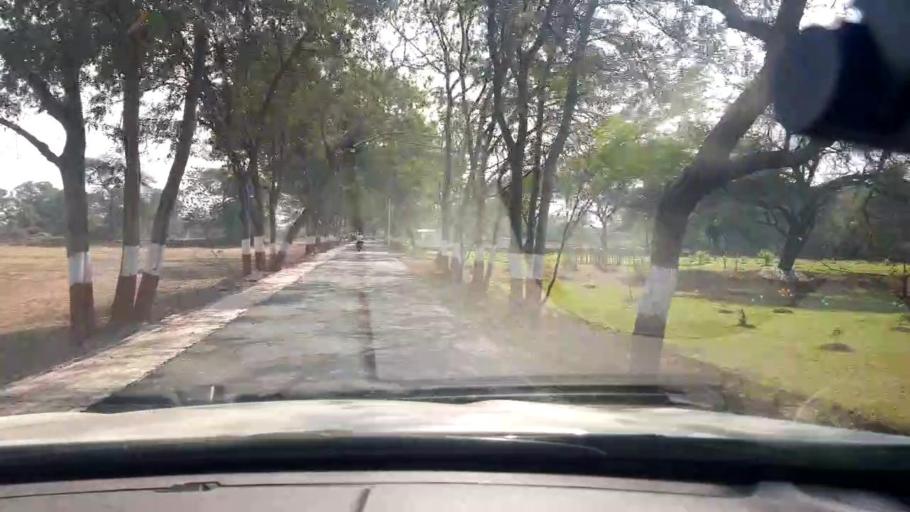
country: IN
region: Maharashtra
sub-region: Pune Division
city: Shivaji Nagar
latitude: 18.5420
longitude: 73.8556
